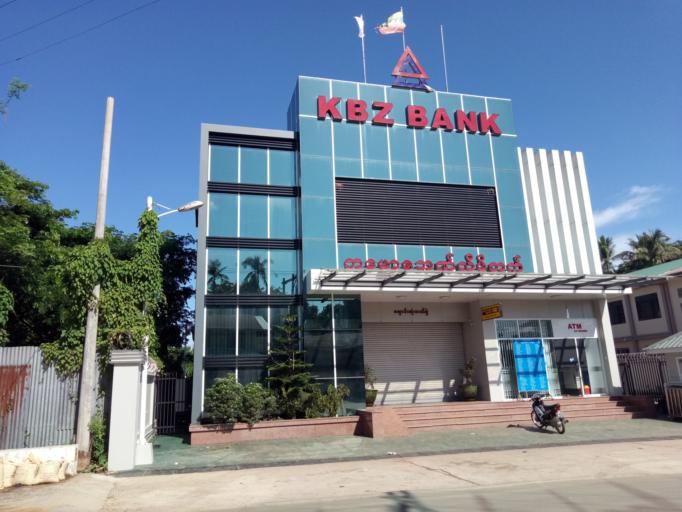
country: MM
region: Mon
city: Mawlamyine
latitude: 16.3552
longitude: 97.5560
